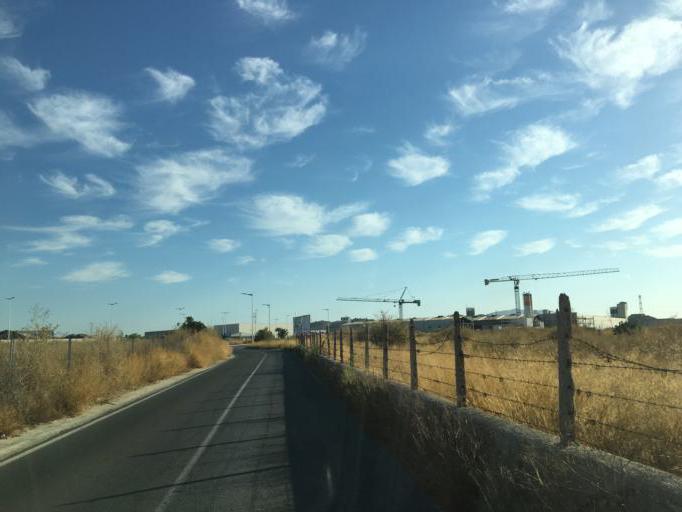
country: ES
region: Murcia
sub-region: Murcia
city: Murcia
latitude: 38.0351
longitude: -1.1192
